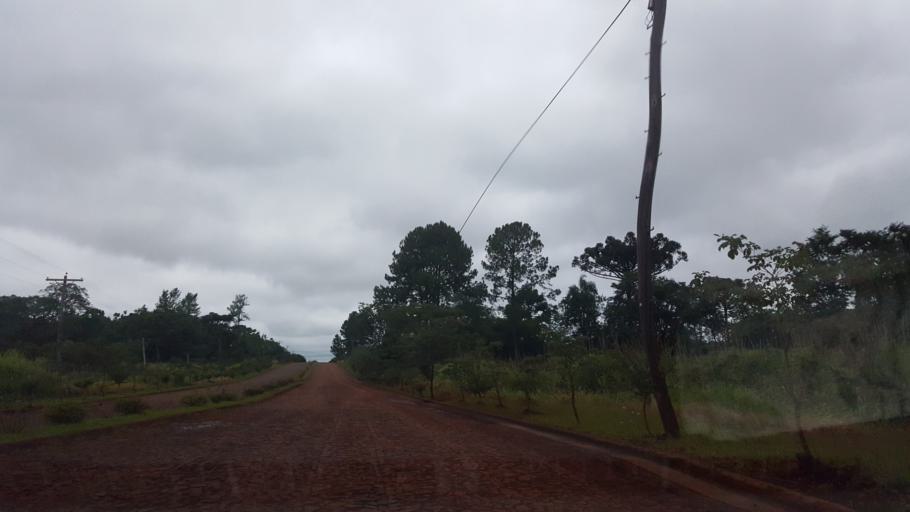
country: AR
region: Misiones
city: Ruiz de Montoya
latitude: -26.9624
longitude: -55.0567
